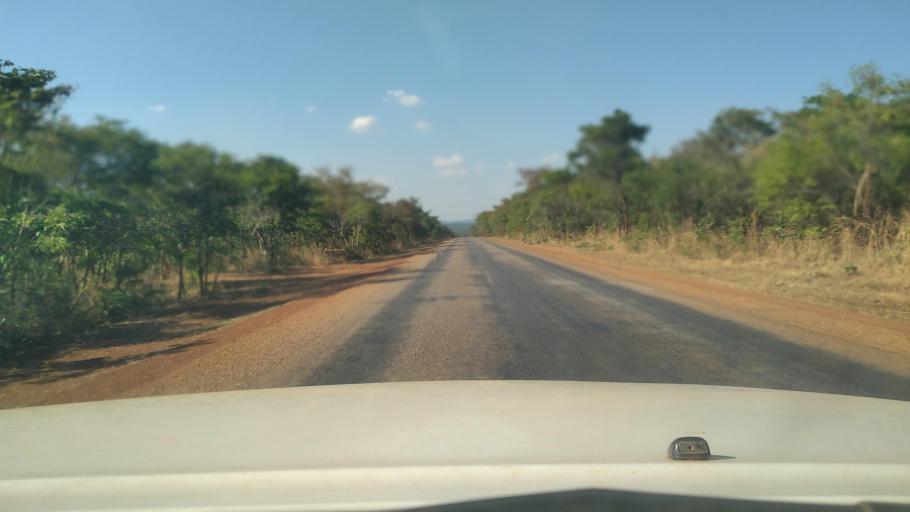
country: ZM
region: Northern
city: Mpika
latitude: -11.7644
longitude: 31.4628
